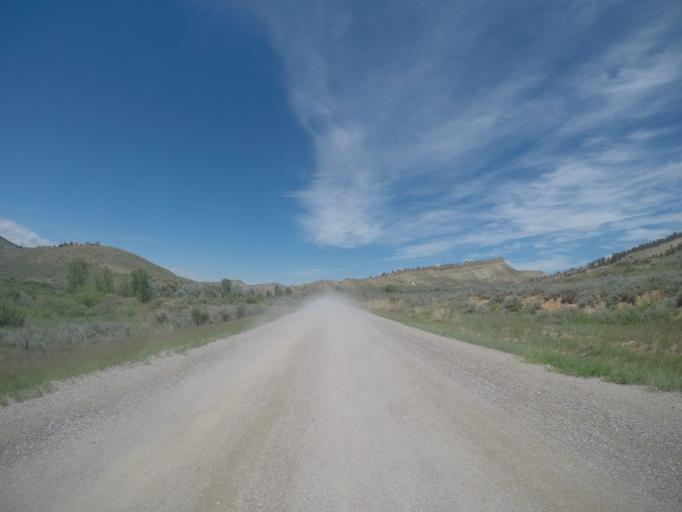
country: US
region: Montana
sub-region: Carbon County
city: Red Lodge
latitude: 45.2077
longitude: -108.8283
